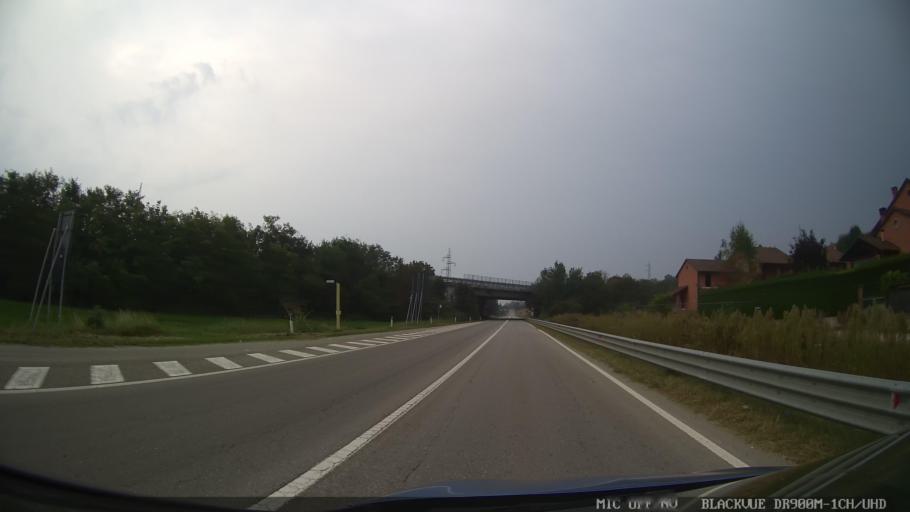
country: IT
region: Piedmont
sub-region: Provincia di Cuneo
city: Fossano
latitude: 44.5714
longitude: 7.7472
